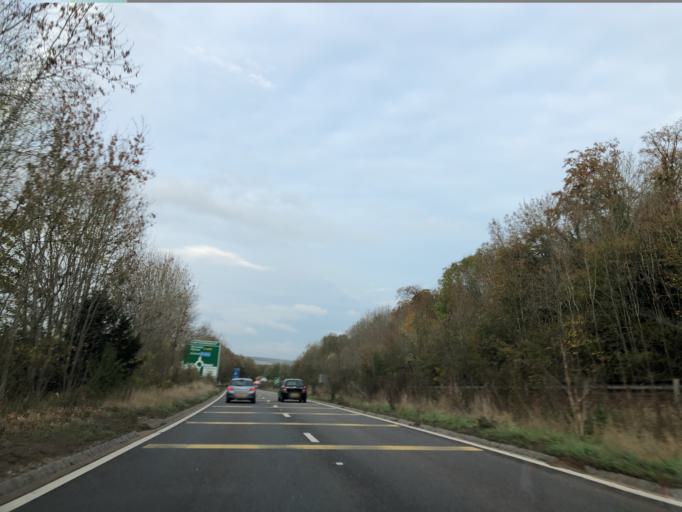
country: GB
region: England
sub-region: Royal Borough of Windsor and Maidenhead
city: Bisham
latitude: 51.5510
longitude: -0.7777
